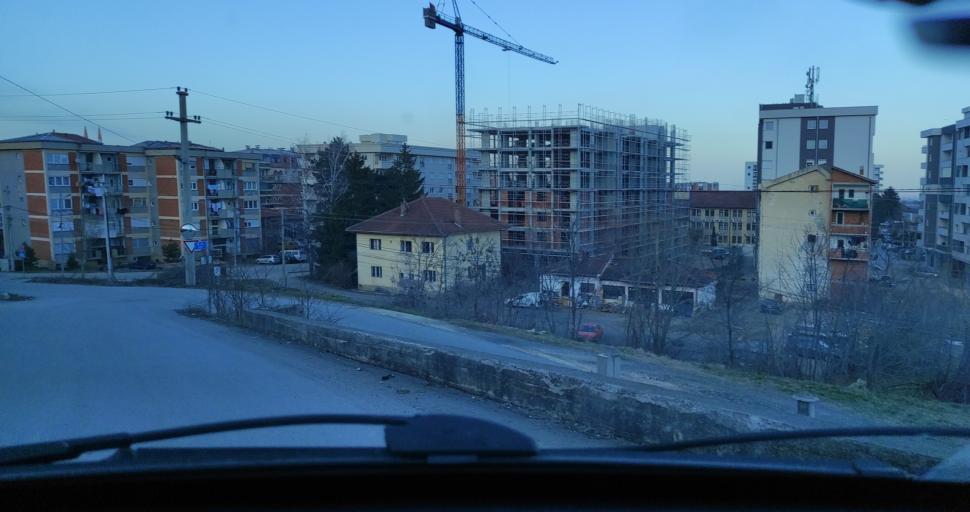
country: XK
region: Gjakova
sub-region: Komuna e Decanit
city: Decan
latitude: 42.5388
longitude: 20.2851
